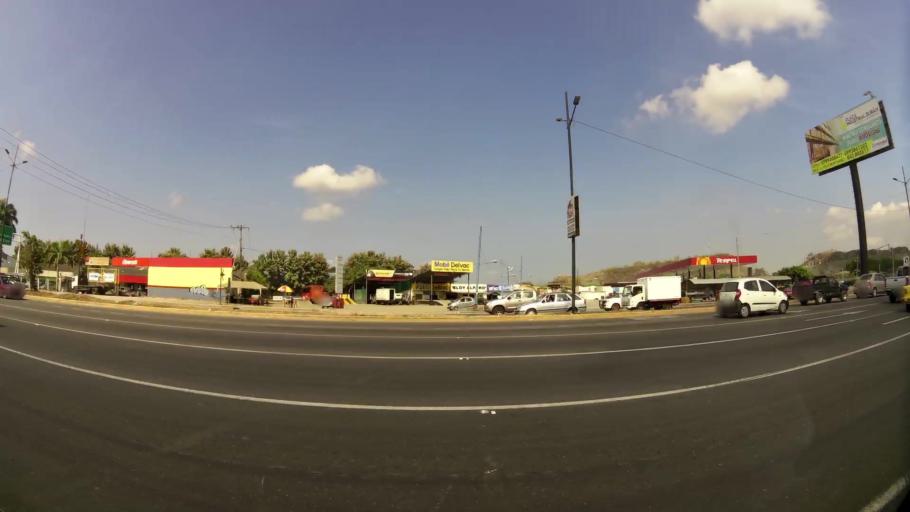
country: EC
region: Guayas
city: Eloy Alfaro
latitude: -2.1753
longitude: -79.8300
